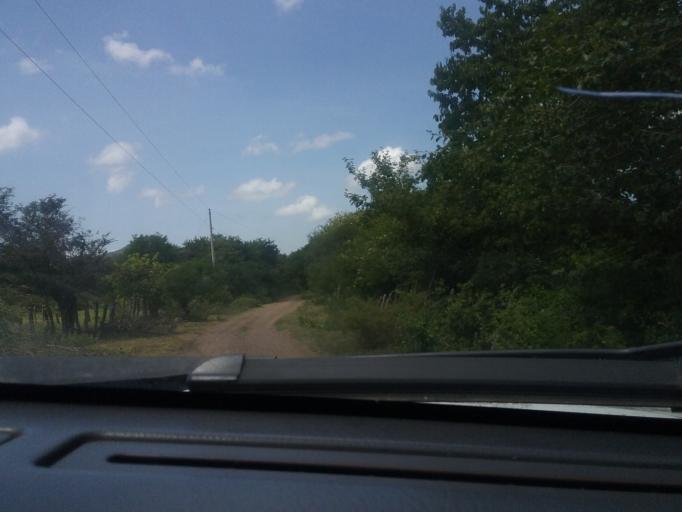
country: NI
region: Matagalpa
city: Terrabona
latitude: 12.6623
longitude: -85.9865
